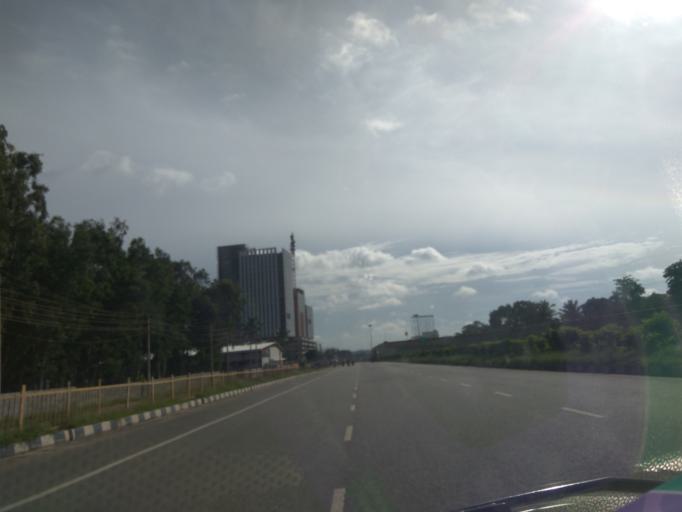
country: IN
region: Karnataka
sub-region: Bangalore Rural
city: Hoskote
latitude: 13.0518
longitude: 77.7586
